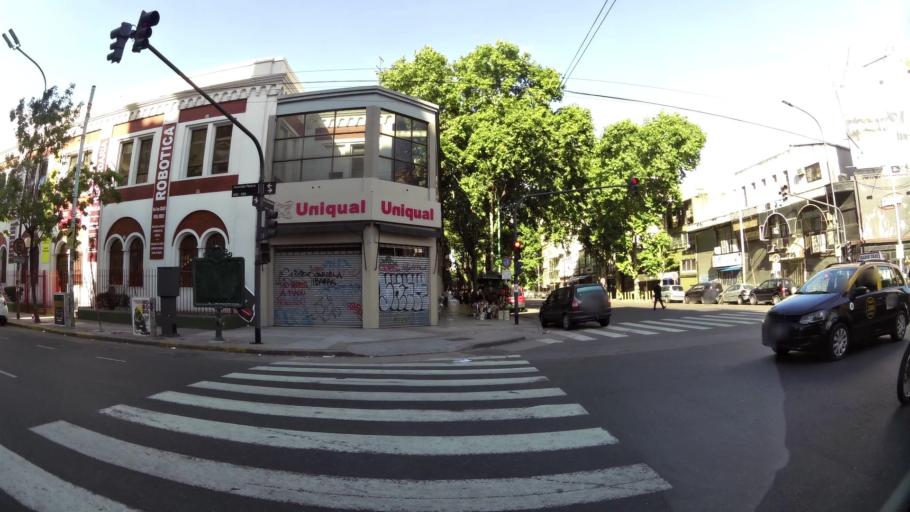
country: AR
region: Buenos Aires F.D.
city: Villa Santa Rita
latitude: -34.6263
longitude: -58.4716
